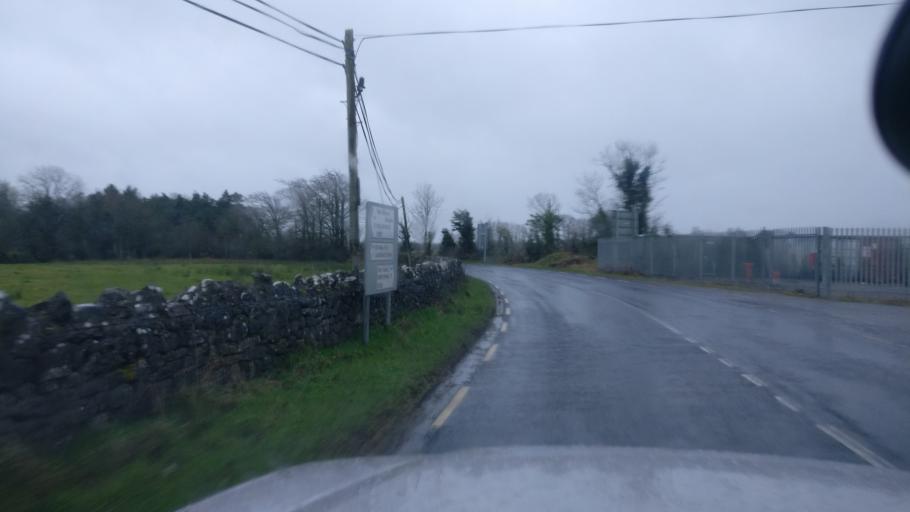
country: IE
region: Connaught
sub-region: County Galway
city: Ballinasloe
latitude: 53.2335
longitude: -8.1900
